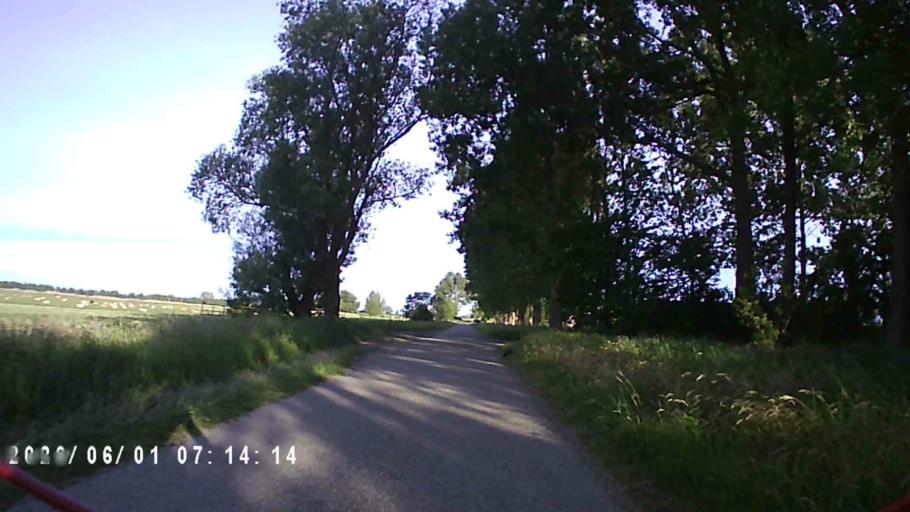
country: NL
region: Friesland
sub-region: Gemeente Dantumadiel
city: Walterswald
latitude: 53.3137
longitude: 6.0527
